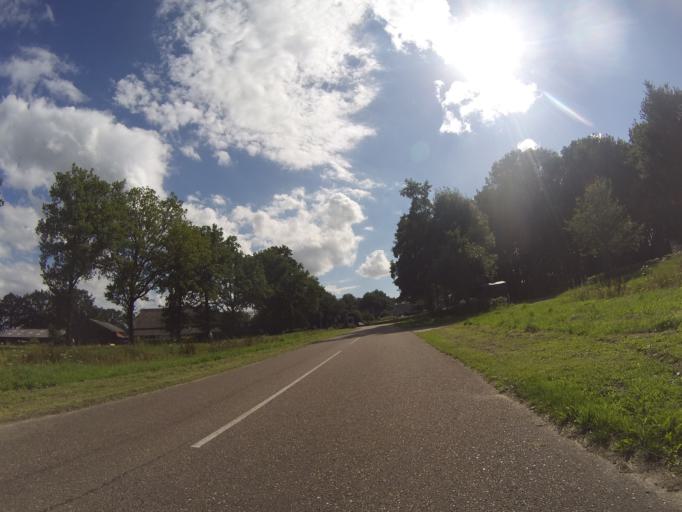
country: NL
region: Drenthe
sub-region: Gemeente Coevorden
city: Dalen
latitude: 52.7269
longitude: 6.7516
